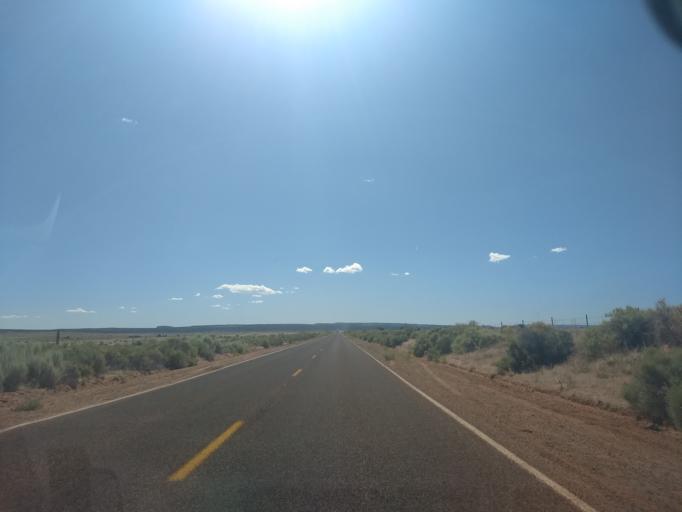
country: US
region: Arizona
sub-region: Mohave County
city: Colorado City
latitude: 36.9469
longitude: -112.9464
